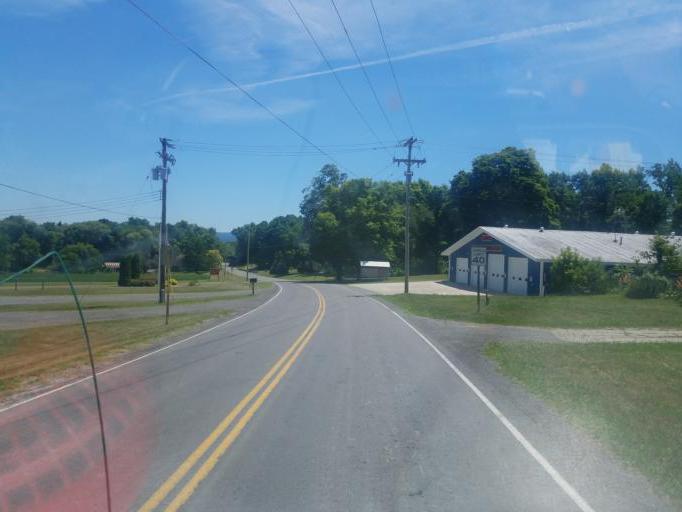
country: US
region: New York
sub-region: Yates County
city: Dundee
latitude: 42.5939
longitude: -76.9597
